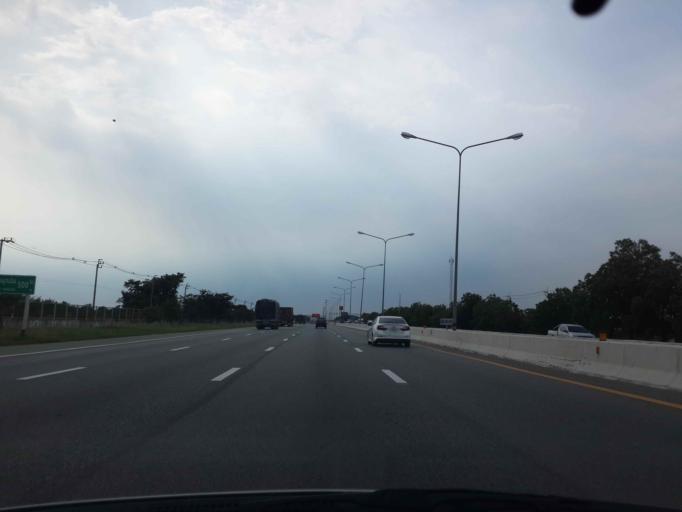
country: TH
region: Samut Prakan
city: Ban Khlong Bang Sao Thong
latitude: 13.6593
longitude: 100.8603
